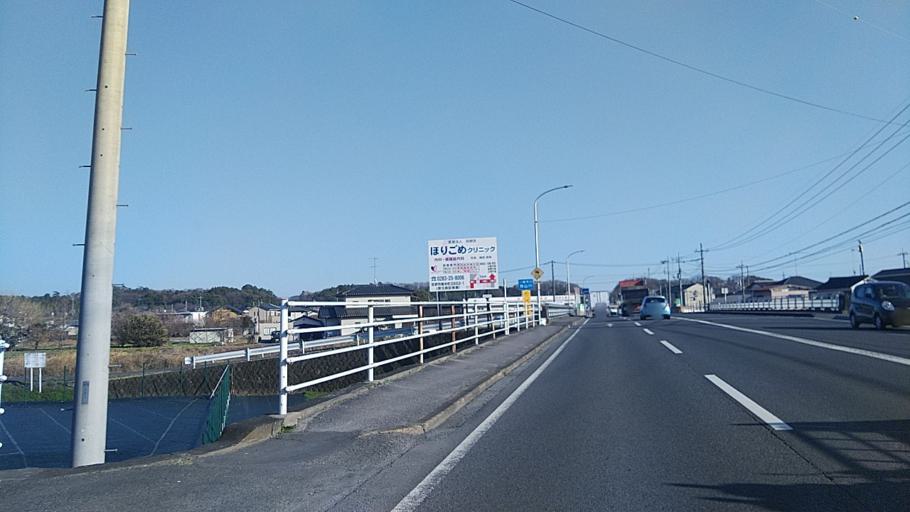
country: JP
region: Tochigi
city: Sano
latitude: 36.3363
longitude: 139.5792
